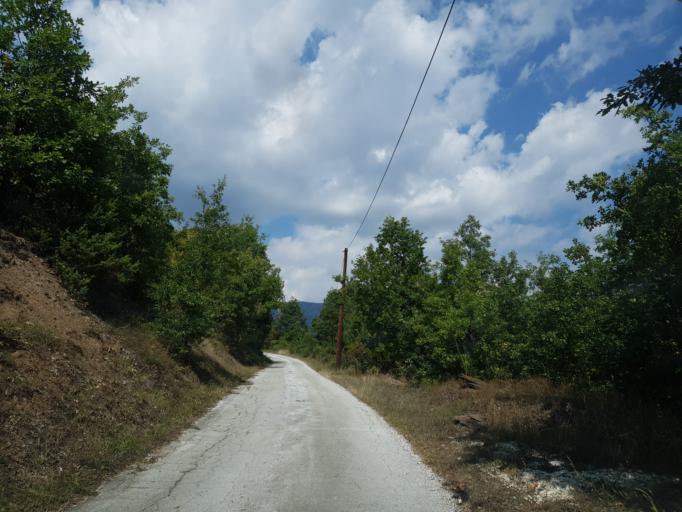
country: MK
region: Makedonski Brod
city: Samokov
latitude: 41.7439
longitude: 21.1057
